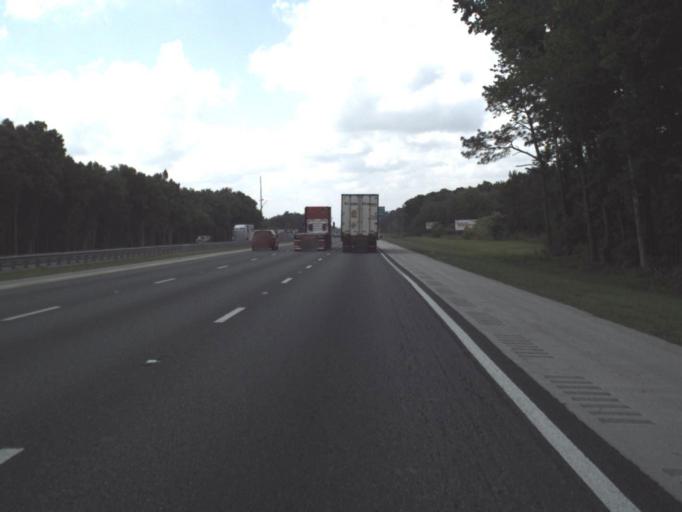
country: US
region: Florida
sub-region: Saint Johns County
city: Villano Beach
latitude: 29.9661
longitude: -81.4496
